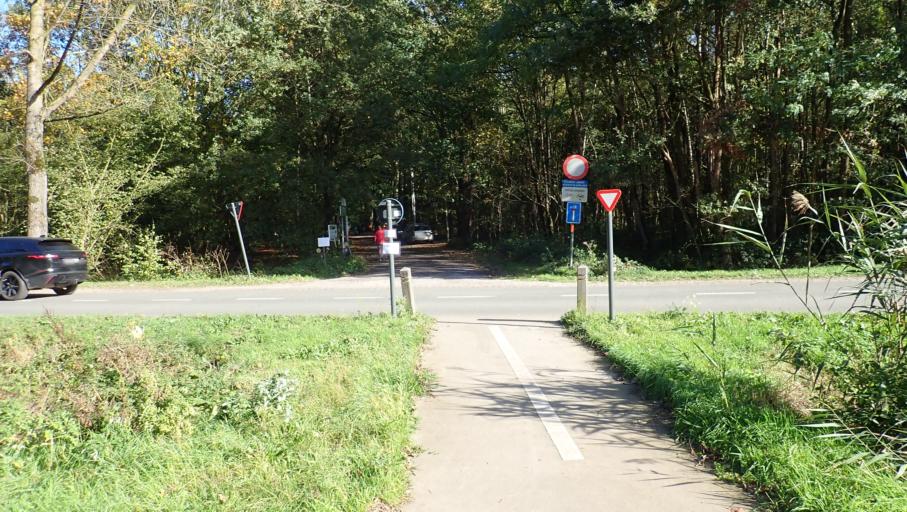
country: BE
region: Flanders
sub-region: Provincie Oost-Vlaanderen
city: Stekene
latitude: 51.1708
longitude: 4.0047
